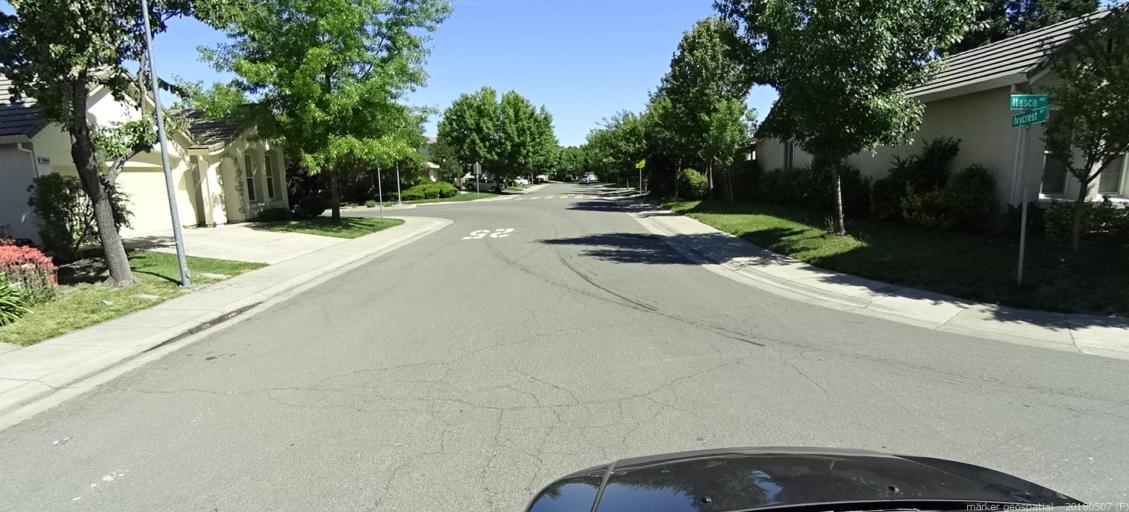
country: US
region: California
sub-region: Sacramento County
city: Rio Linda
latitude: 38.6575
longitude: -121.5022
